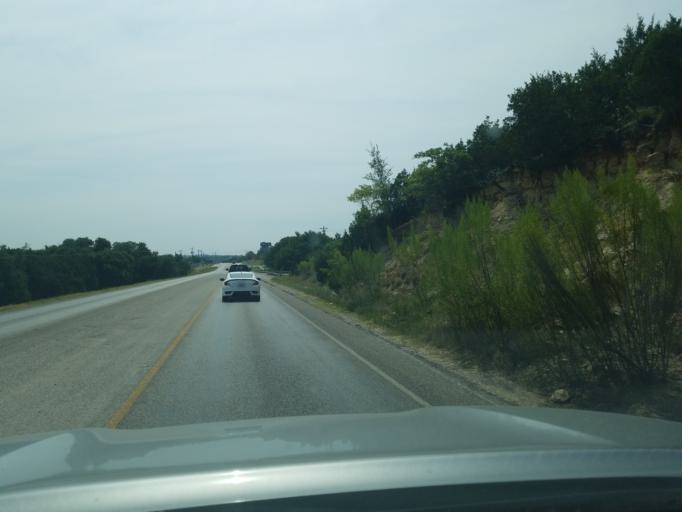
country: US
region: Texas
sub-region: Comal County
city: Bulverde
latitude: 29.7993
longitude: -98.4345
